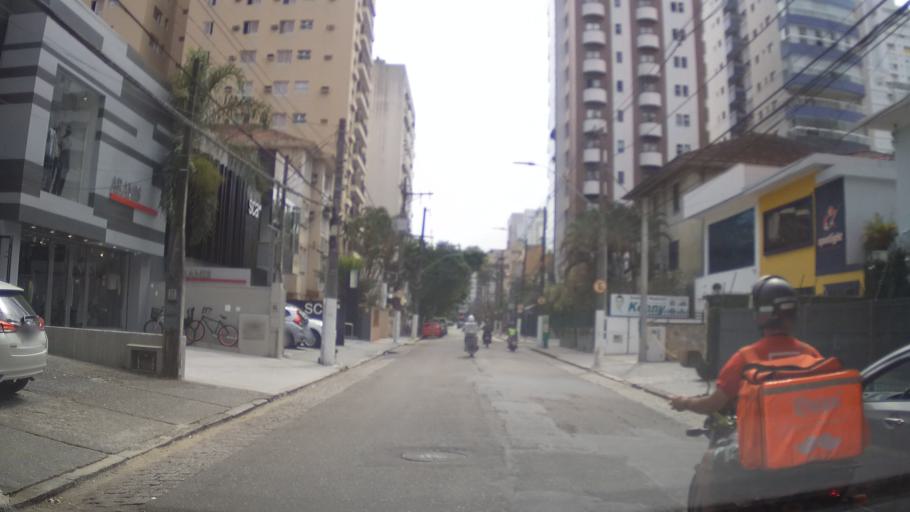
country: BR
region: Sao Paulo
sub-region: Santos
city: Santos
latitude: -23.9666
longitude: -46.3242
